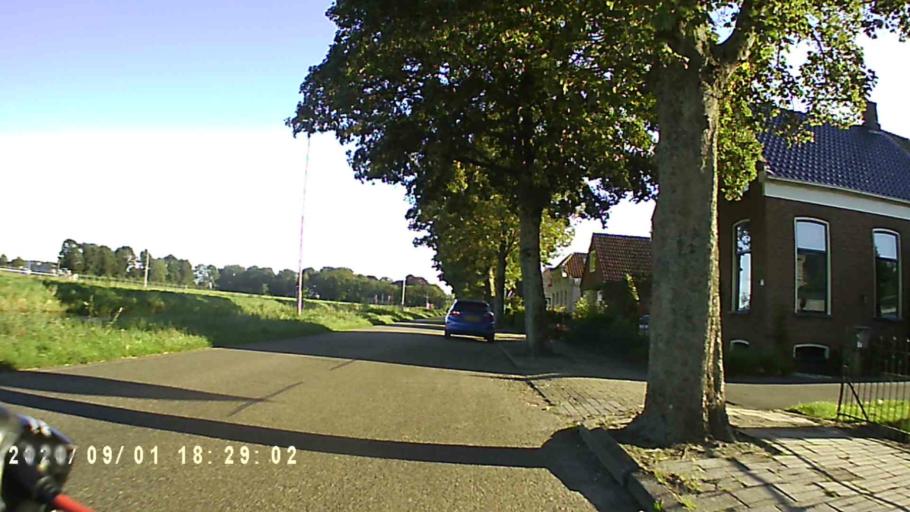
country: NL
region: Groningen
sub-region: Gemeente Hoogezand-Sappemeer
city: Sappemeer
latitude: 53.1580
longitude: 6.7962
